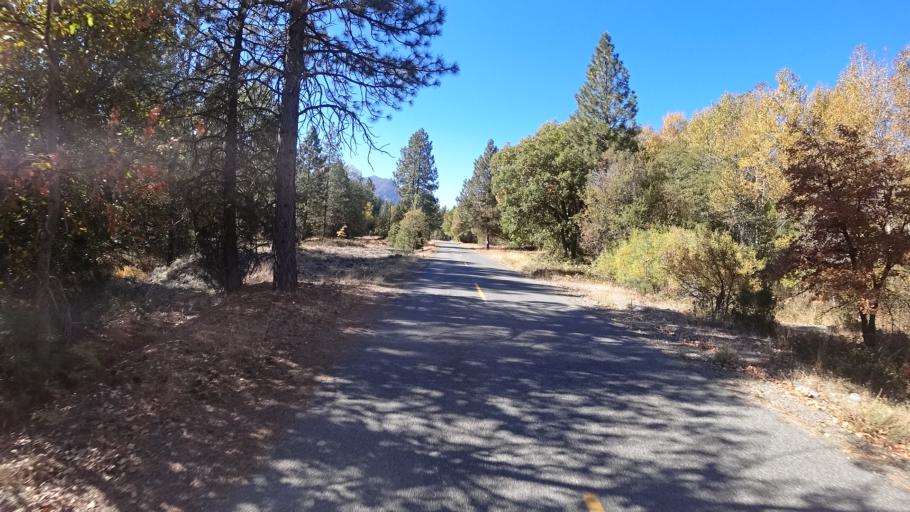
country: US
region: California
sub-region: Siskiyou County
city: Yreka
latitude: 41.5344
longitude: -122.9390
